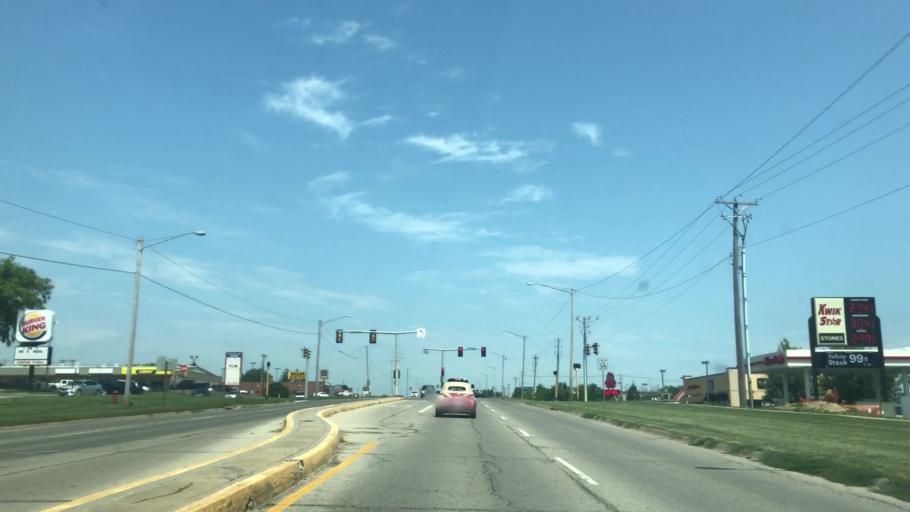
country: US
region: Iowa
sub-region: Marshall County
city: Marshalltown
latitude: 42.0148
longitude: -92.9123
